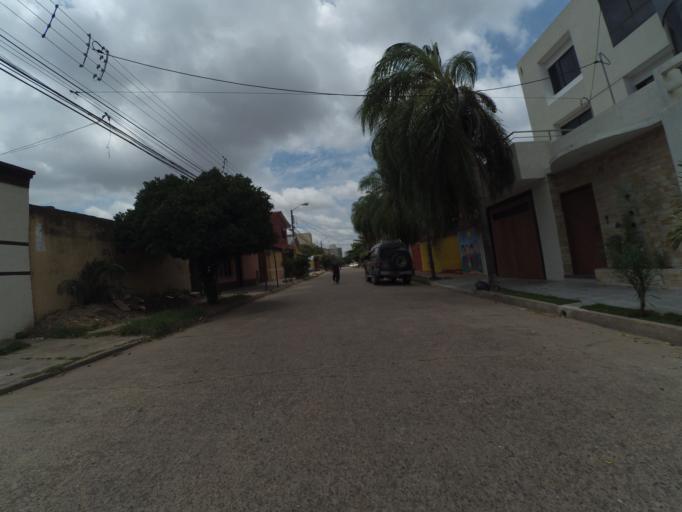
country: BO
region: Santa Cruz
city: Santa Cruz de la Sierra
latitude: -17.7888
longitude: -63.1980
